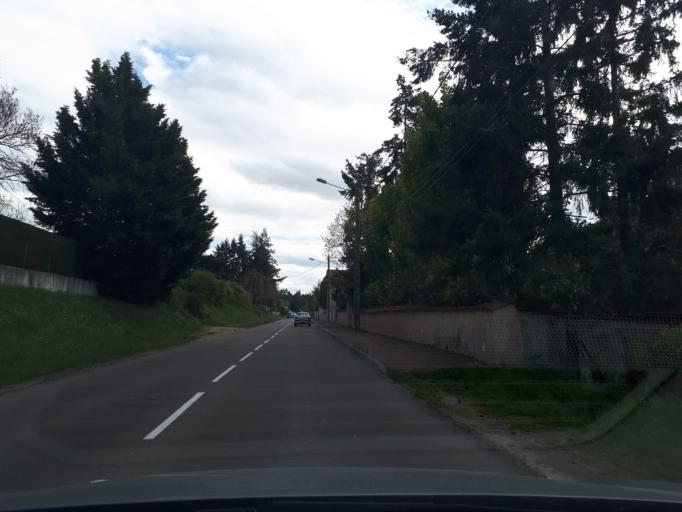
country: FR
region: Rhone-Alpes
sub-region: Departement de la Loire
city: Saint-Galmier
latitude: 45.6079
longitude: 4.3126
